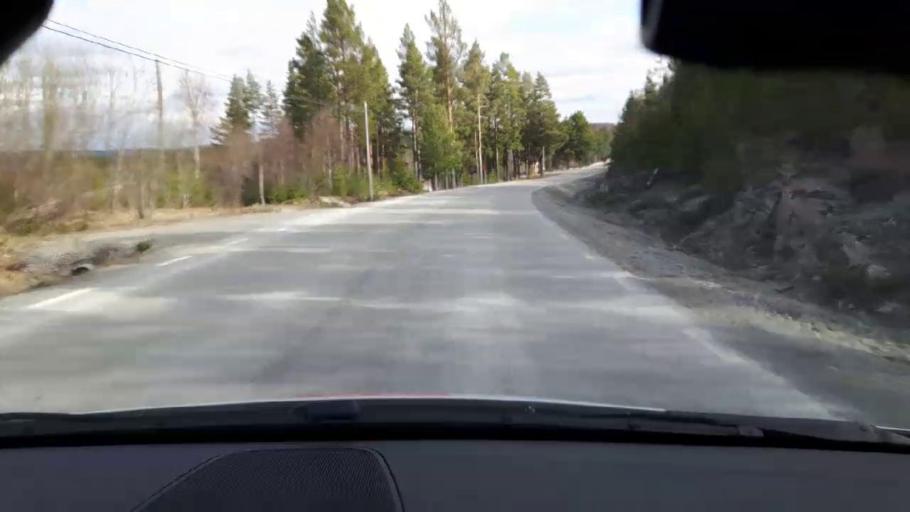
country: SE
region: Jaemtland
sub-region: Bergs Kommun
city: Hoverberg
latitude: 62.7342
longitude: 14.5944
